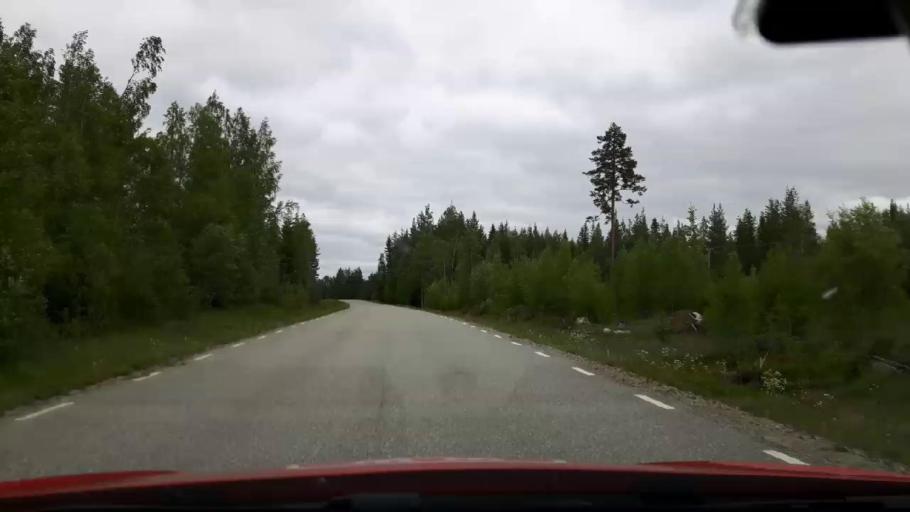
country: SE
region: Jaemtland
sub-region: Ragunda Kommun
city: Hammarstrand
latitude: 63.2097
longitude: 16.0063
